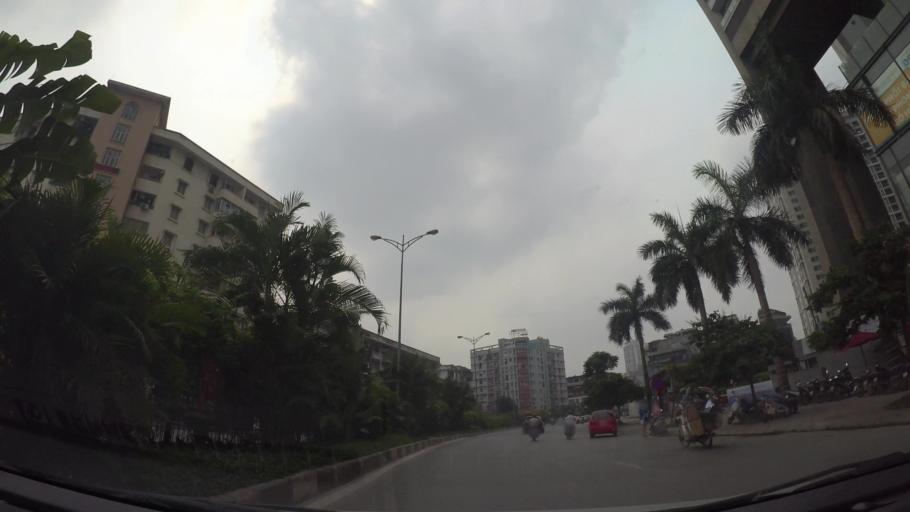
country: VN
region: Ha Noi
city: Cau Dien
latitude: 21.0293
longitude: 105.7764
